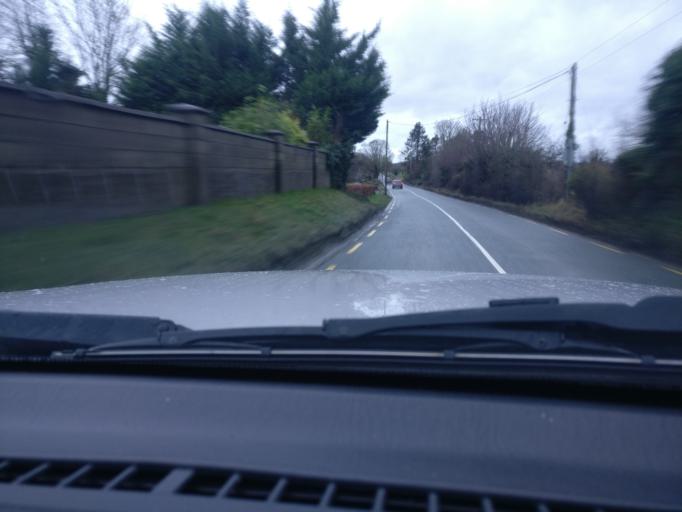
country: IE
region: Leinster
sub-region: An Mhi
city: Longwood
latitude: 53.5001
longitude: -6.8563
